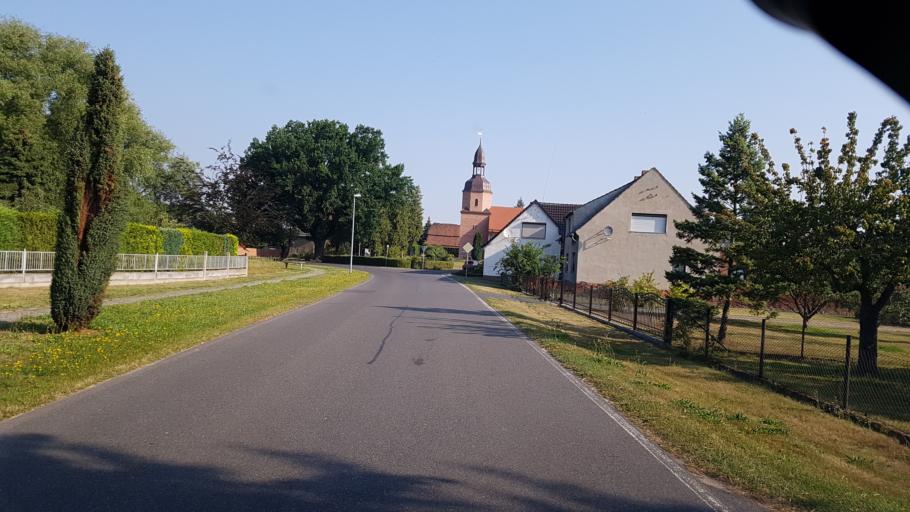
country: DE
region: Brandenburg
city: Drebkau
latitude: 51.6709
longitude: 14.2330
